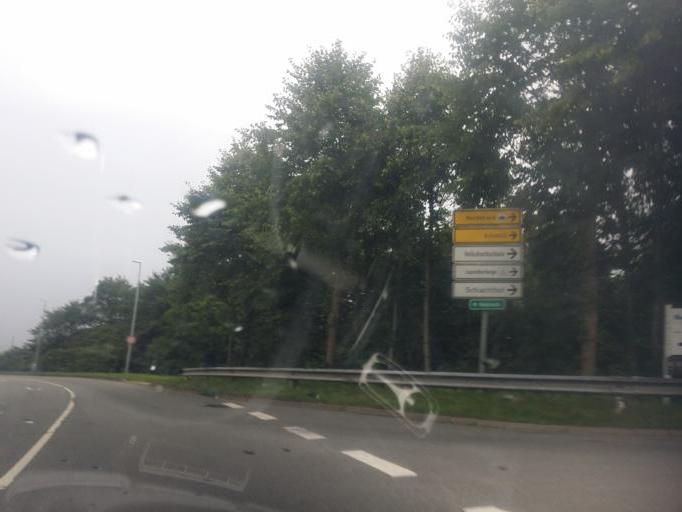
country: DE
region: Schleswig-Holstein
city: Husum
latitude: 54.4857
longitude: 9.0431
